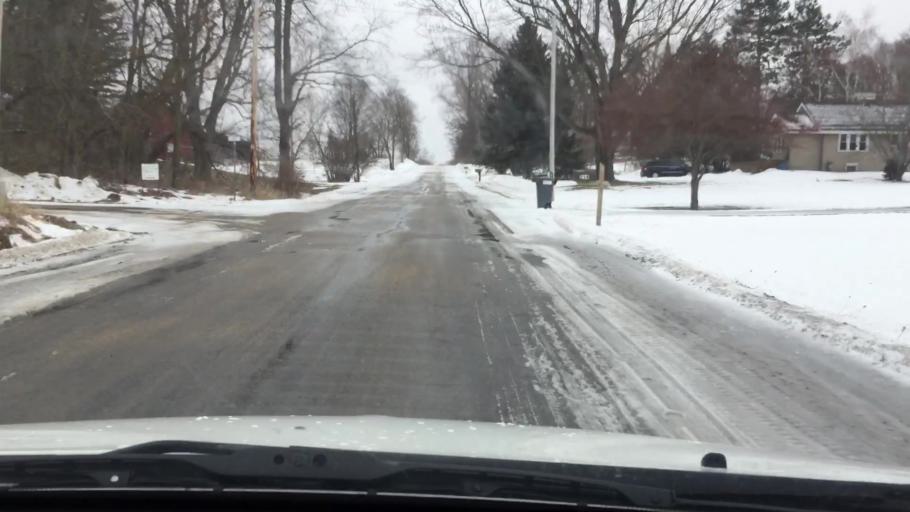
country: US
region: Michigan
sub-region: Osceola County
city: Reed City
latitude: 44.0347
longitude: -85.4539
